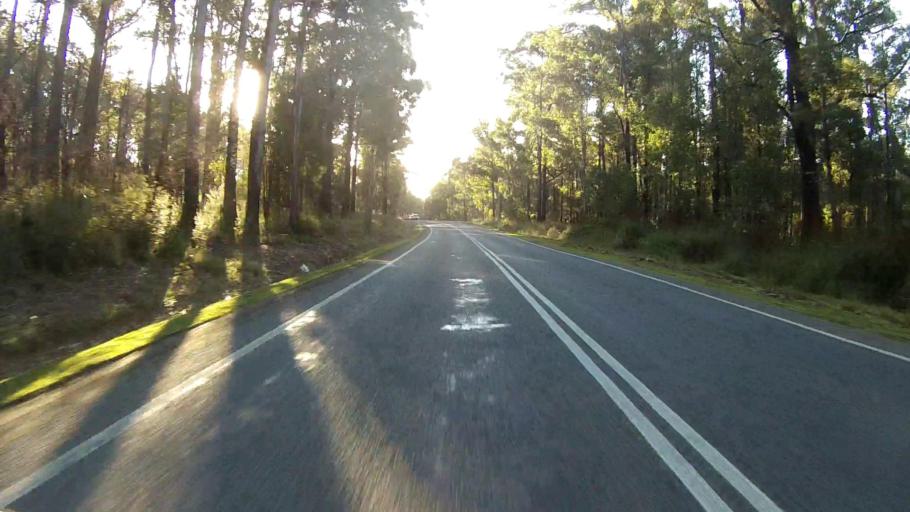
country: AU
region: Tasmania
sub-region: Sorell
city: Sorell
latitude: -42.9764
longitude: 147.9070
